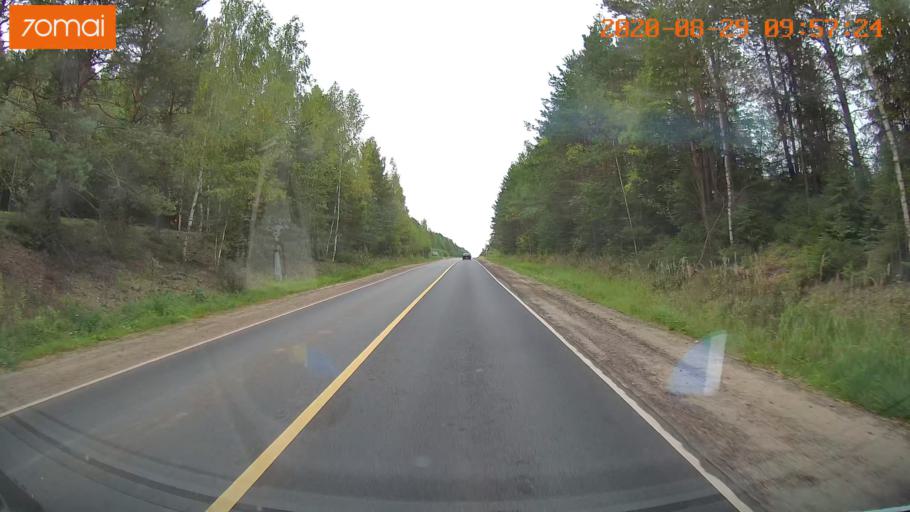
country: RU
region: Ivanovo
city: Zarechnyy
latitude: 57.4165
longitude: 42.3130
